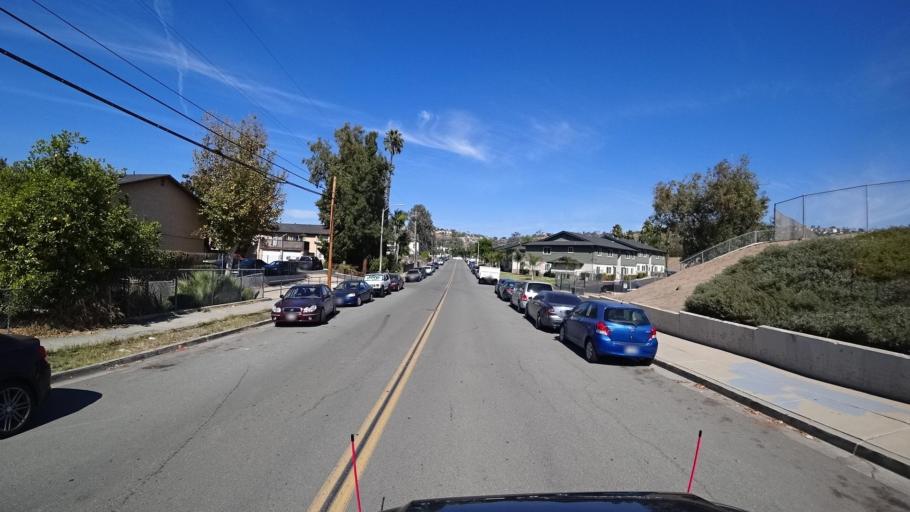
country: US
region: California
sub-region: San Diego County
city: La Presa
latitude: 32.7129
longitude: -117.0060
